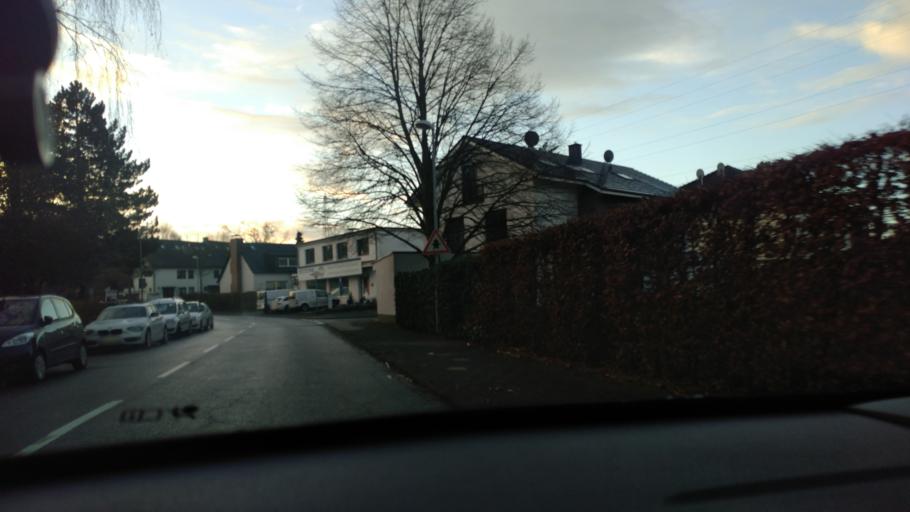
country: DE
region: North Rhine-Westphalia
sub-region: Regierungsbezirk Dusseldorf
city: Muelheim (Ruhr)
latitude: 51.4037
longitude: 6.8607
